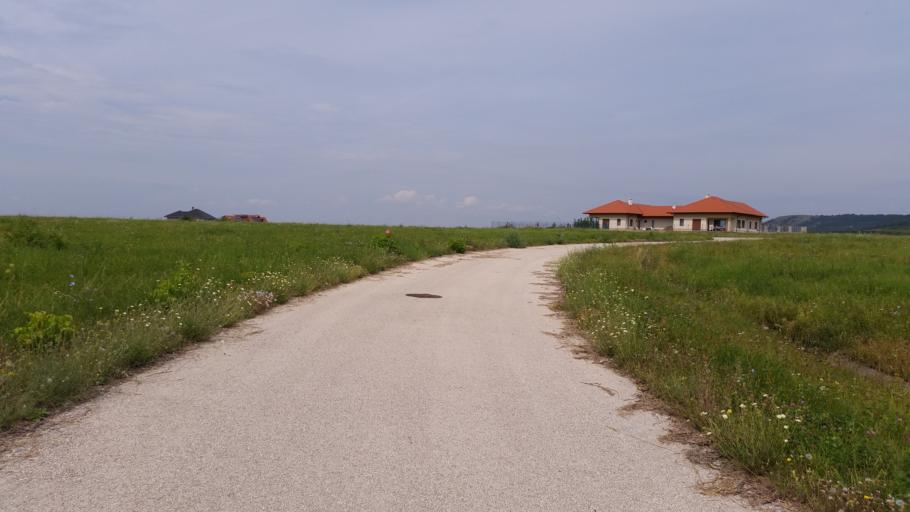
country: HU
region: Pest
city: Telki
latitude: 47.5602
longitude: 18.8103
